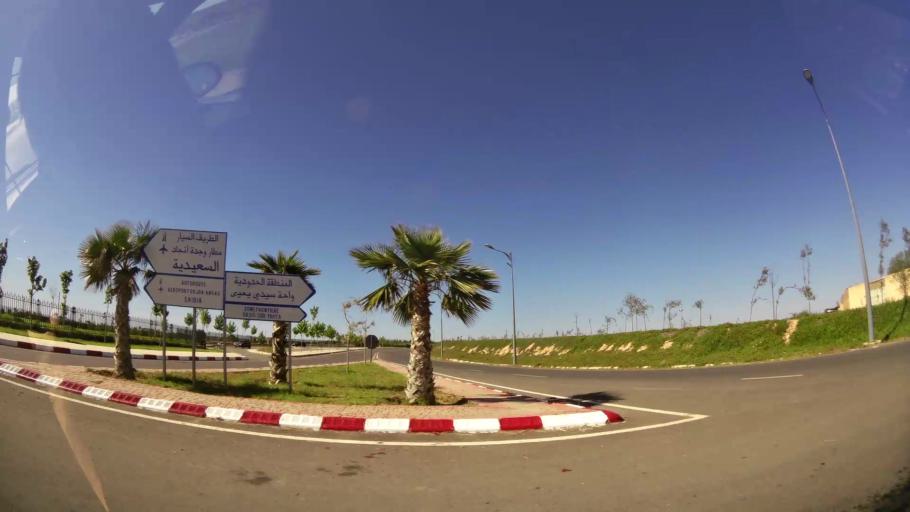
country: MA
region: Oriental
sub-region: Oujda-Angad
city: Oujda
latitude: 34.7375
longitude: -1.9190
